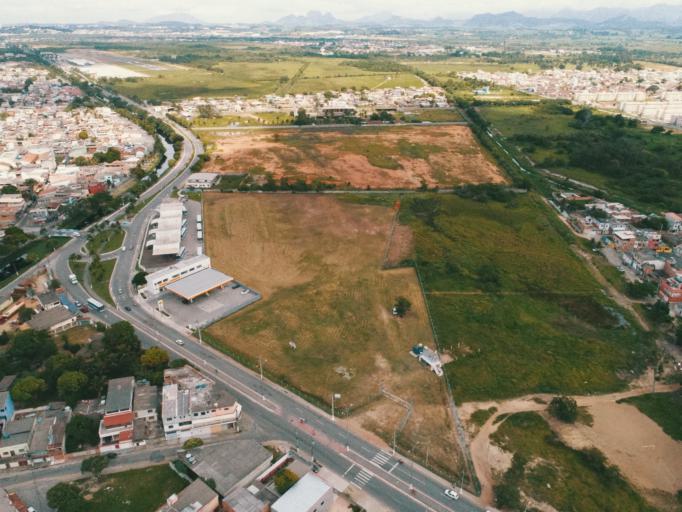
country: BR
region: Rio de Janeiro
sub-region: Macae
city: Macae
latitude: -22.3293
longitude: -41.7512
